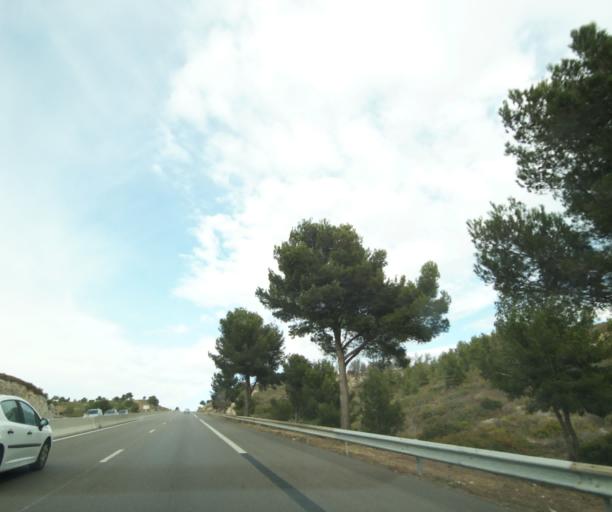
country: FR
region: Provence-Alpes-Cote d'Azur
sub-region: Departement des Bouches-du-Rhone
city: Carry-le-Rouet
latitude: 43.3457
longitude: 5.1698
